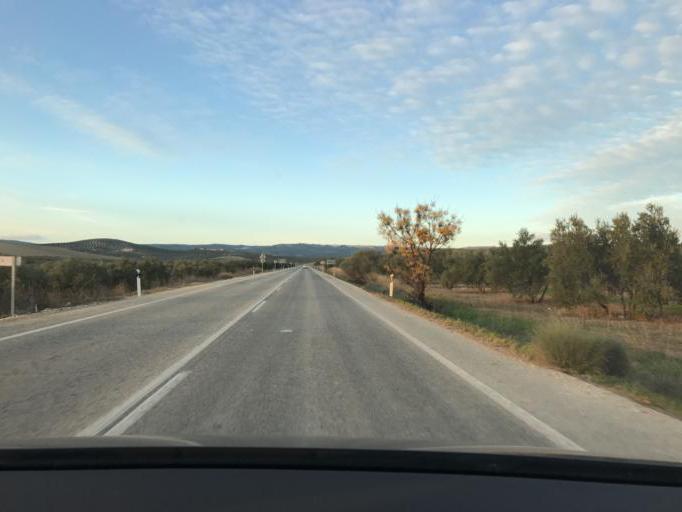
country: ES
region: Andalusia
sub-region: Provincia de Jaen
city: Ubeda
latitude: 37.9341
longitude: -3.3555
